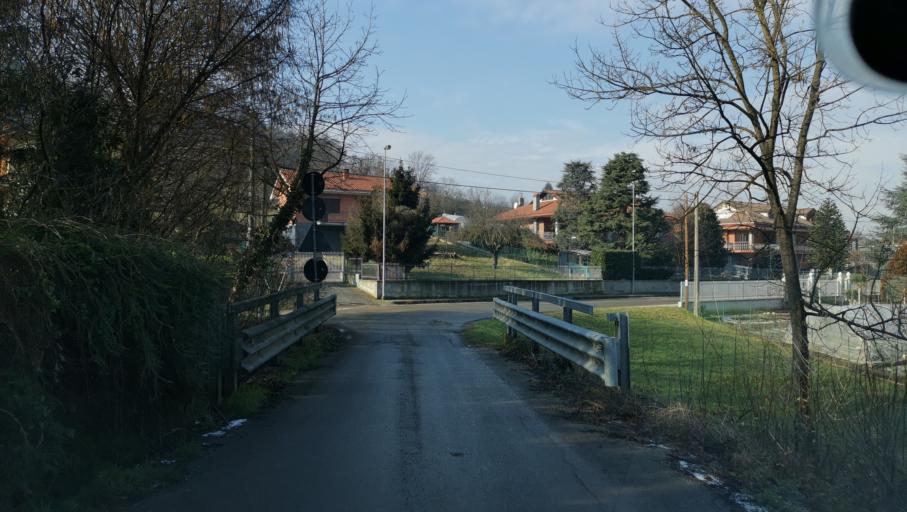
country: IT
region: Piedmont
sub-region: Provincia di Torino
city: Gassino Torinese
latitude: 45.1209
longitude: 7.8323
